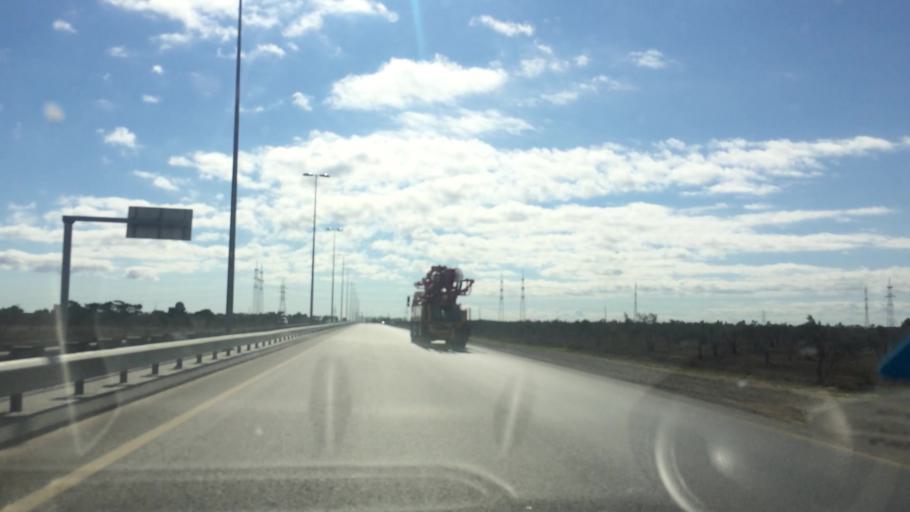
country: AZ
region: Baki
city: Qala
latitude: 40.4421
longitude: 50.1799
